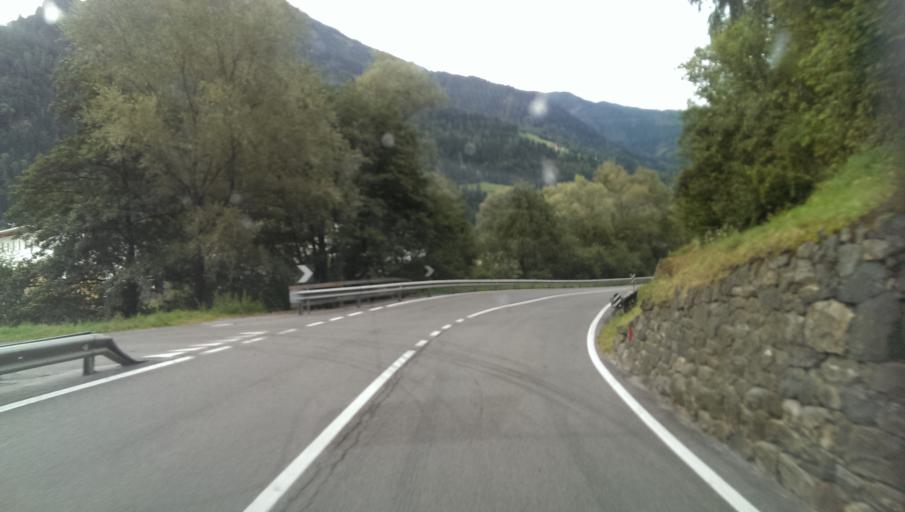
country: IT
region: Trentino-Alto Adige
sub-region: Bolzano
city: San Martino in Passiria
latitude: 46.7914
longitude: 11.2308
